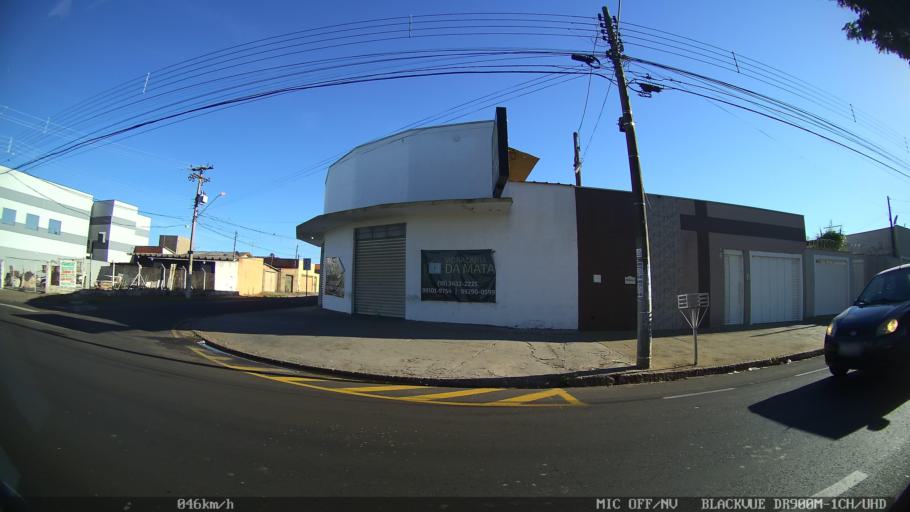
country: BR
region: Sao Paulo
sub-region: Franca
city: Franca
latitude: -20.5821
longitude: -47.3820
